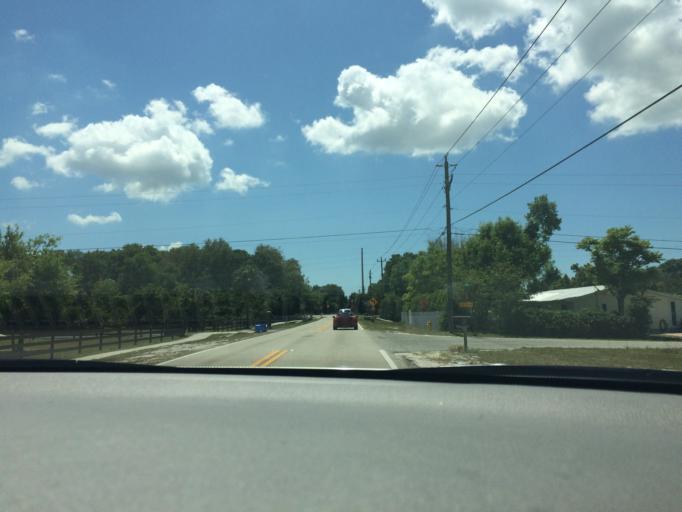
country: US
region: Florida
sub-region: Manatee County
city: Samoset
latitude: 27.4638
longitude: -82.4895
